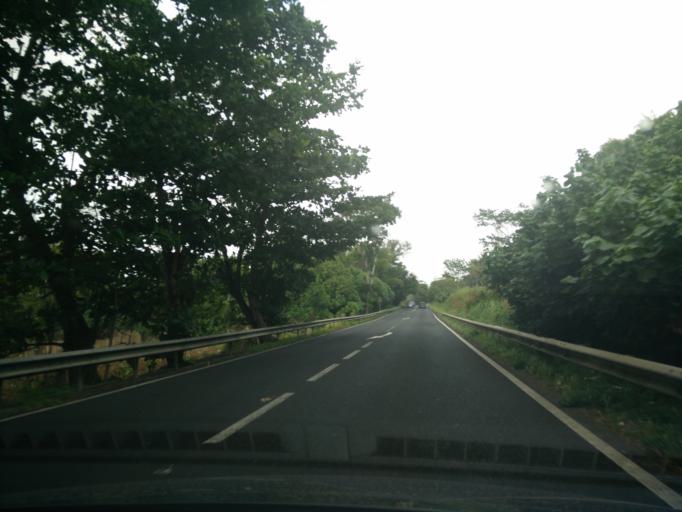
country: GP
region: Guadeloupe
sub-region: Guadeloupe
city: Petit-Bourg
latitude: 16.2150
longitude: -61.6199
